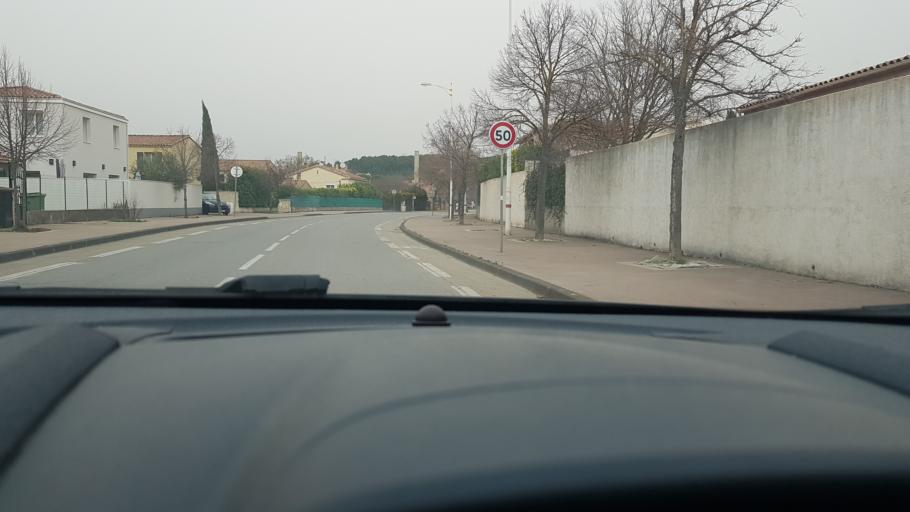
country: FR
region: Provence-Alpes-Cote d'Azur
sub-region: Departement des Bouches-du-Rhone
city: Gardanne
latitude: 43.4500
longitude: 5.4727
